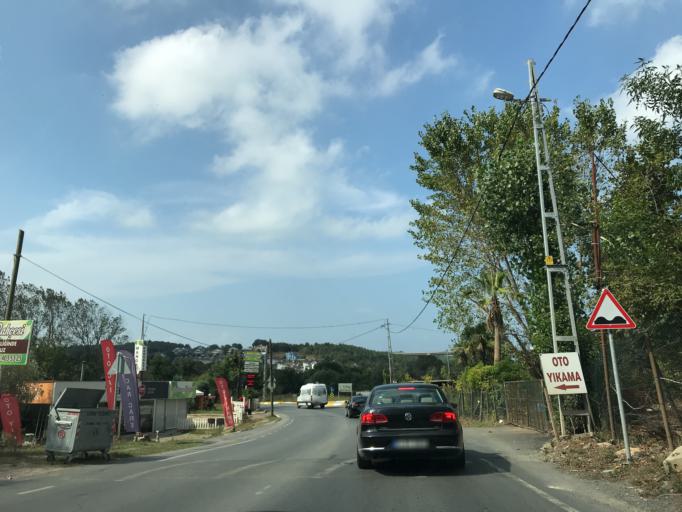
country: TR
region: Istanbul
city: Arikoey
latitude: 41.2181
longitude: 29.0349
